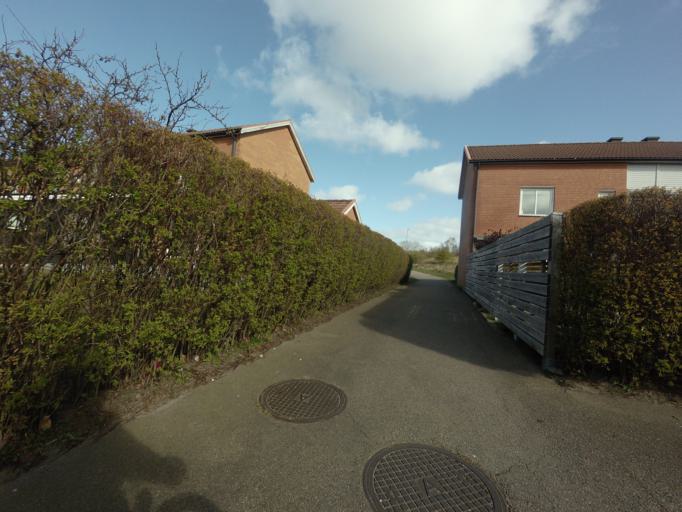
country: SE
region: Skane
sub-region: Hoganas Kommun
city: Hoganas
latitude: 56.1764
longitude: 12.5717
